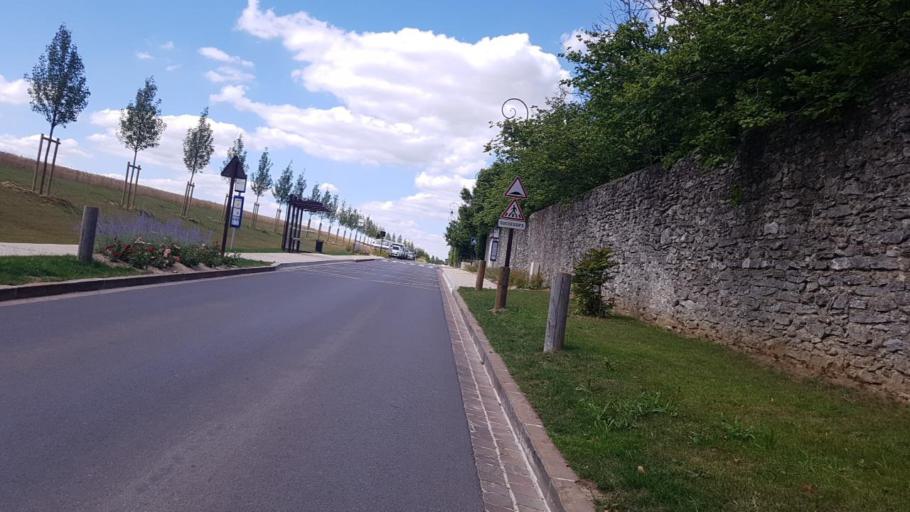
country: FR
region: Ile-de-France
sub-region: Departement de Seine-et-Marne
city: Longperrier
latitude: 49.0205
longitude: 2.6476
